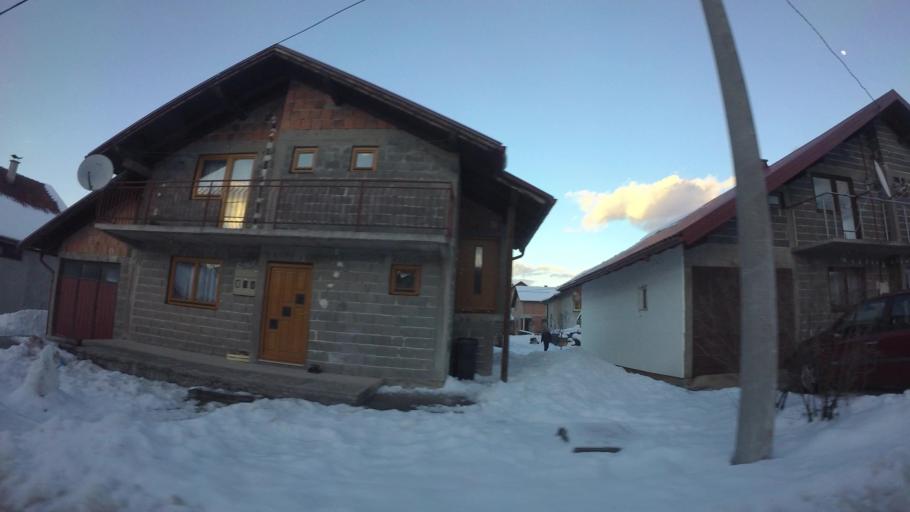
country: BA
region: Federation of Bosnia and Herzegovina
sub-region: Kanton Sarajevo
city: Sarajevo
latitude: 43.8065
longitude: 18.3723
